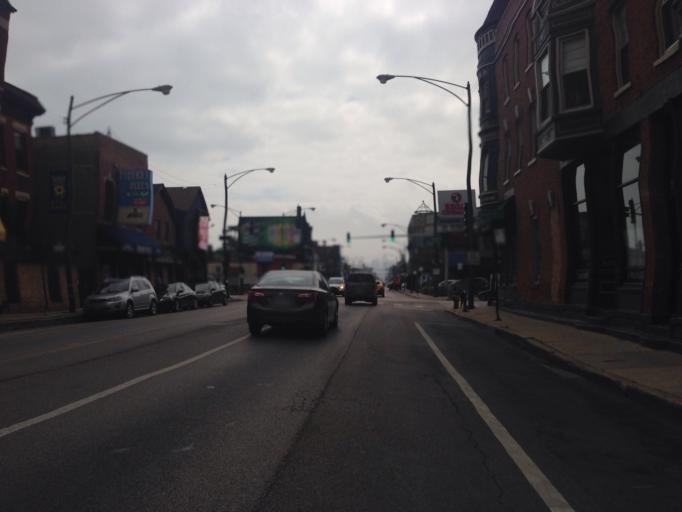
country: US
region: Illinois
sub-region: Cook County
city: Chicago
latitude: 41.9221
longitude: -87.6652
